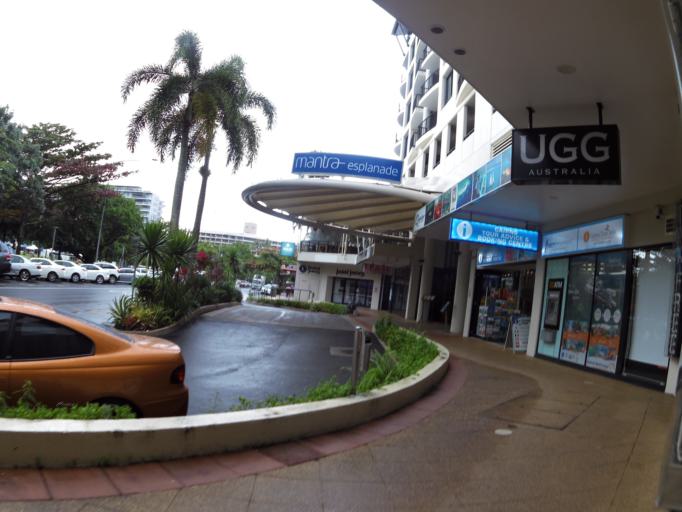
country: AU
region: Queensland
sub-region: Cairns
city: Cairns
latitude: -16.9209
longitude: 145.7781
